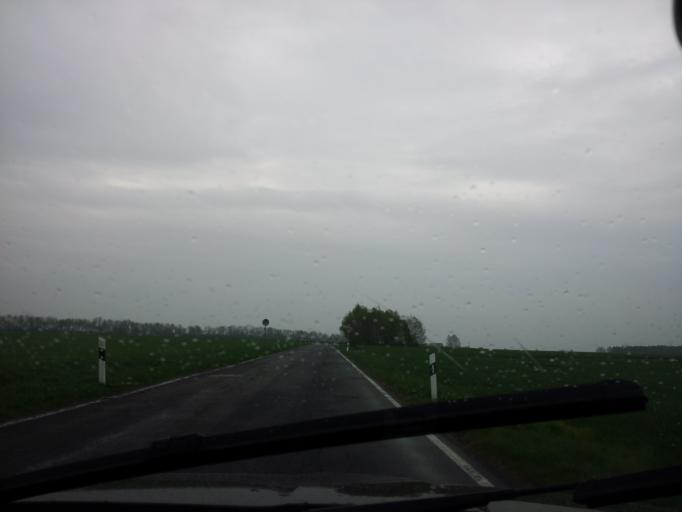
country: DE
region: Saxony-Anhalt
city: Kropstadt
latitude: 51.9808
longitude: 12.8162
